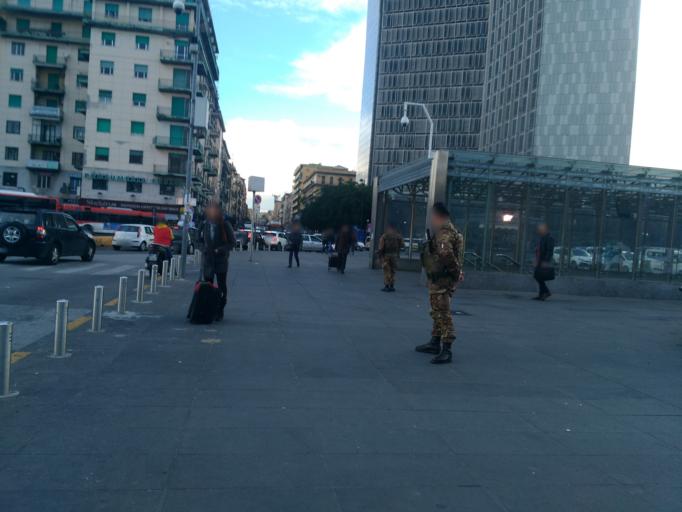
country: IT
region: Campania
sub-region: Provincia di Napoli
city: Napoli
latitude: 40.8526
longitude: 14.2717
